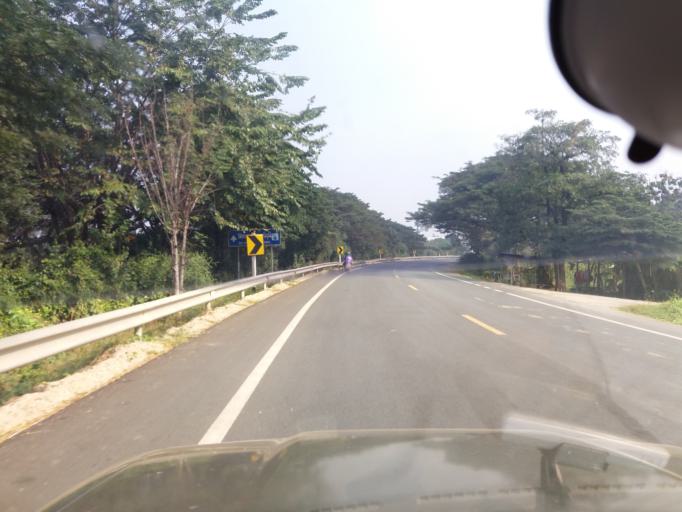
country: TH
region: Sing Buri
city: Bang Racham
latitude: 14.9261
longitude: 100.2678
